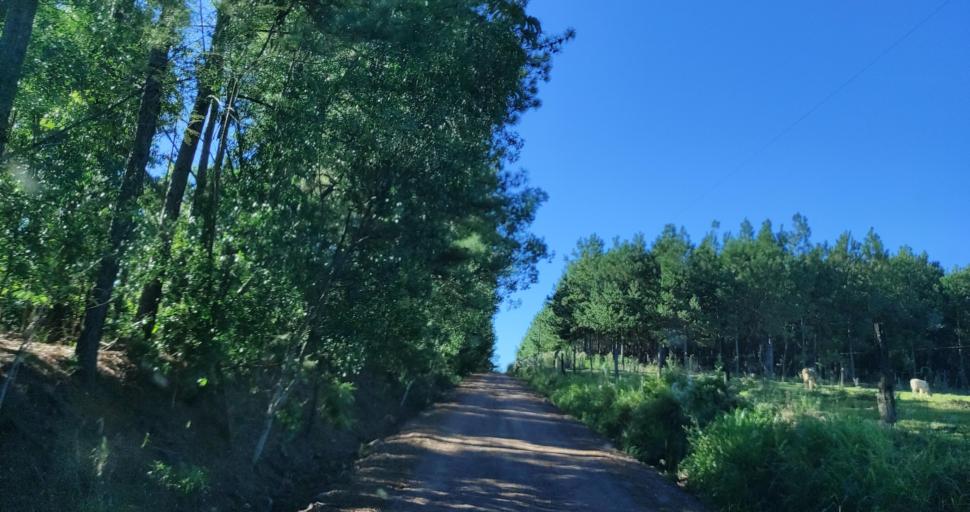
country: AR
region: Misiones
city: Capiovi
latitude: -26.9194
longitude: -55.0002
